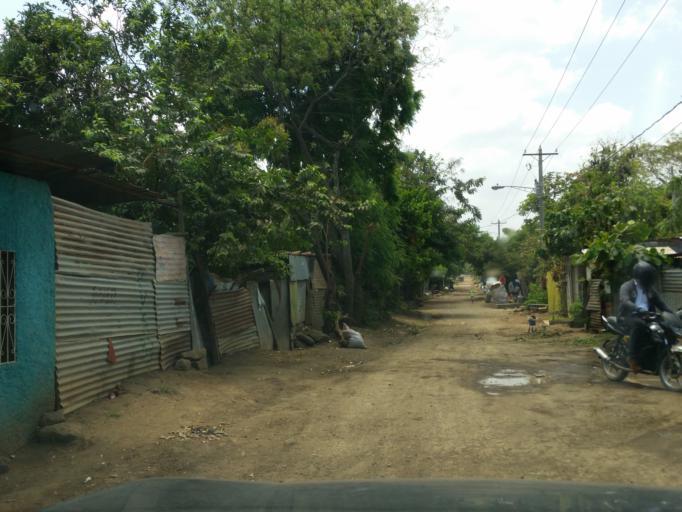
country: NI
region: Managua
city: Managua
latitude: 12.1429
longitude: -86.1911
